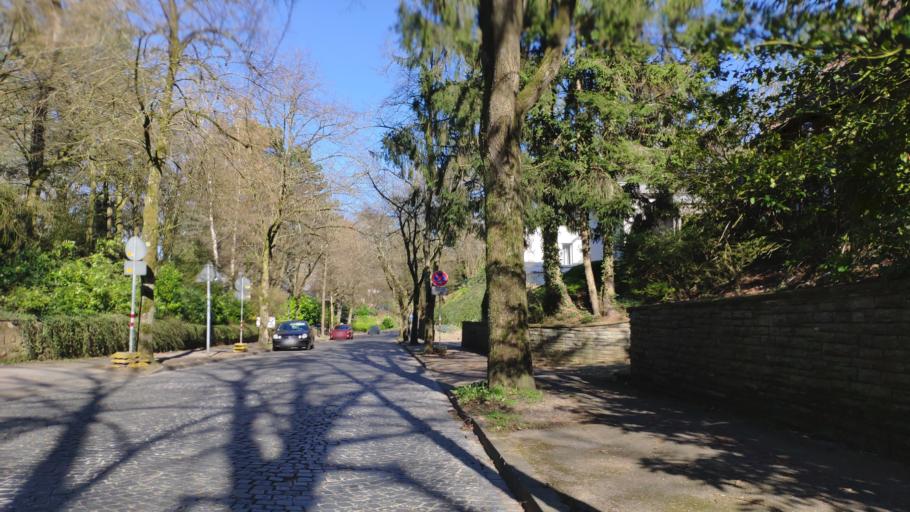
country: DE
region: North Rhine-Westphalia
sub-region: Regierungsbezirk Koln
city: Aachen
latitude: 50.8029
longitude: 6.0550
